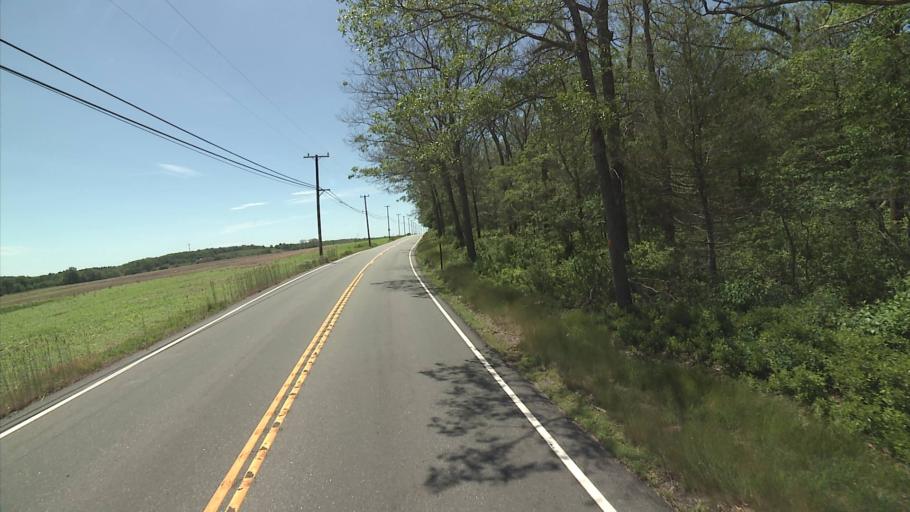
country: US
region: Rhode Island
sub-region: Washington County
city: Hopkinton
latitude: 41.5454
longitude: -71.8430
